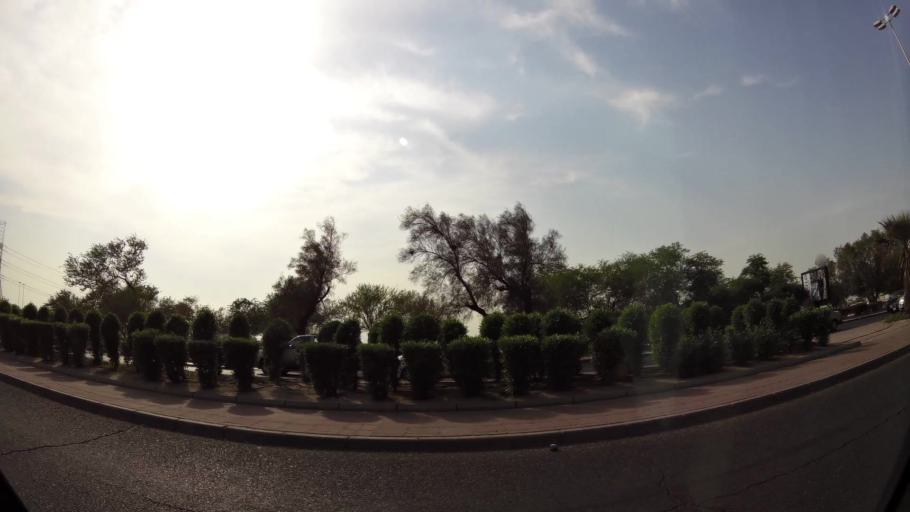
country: KW
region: Al Farwaniyah
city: Al Farwaniyah
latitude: 29.3067
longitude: 47.9629
